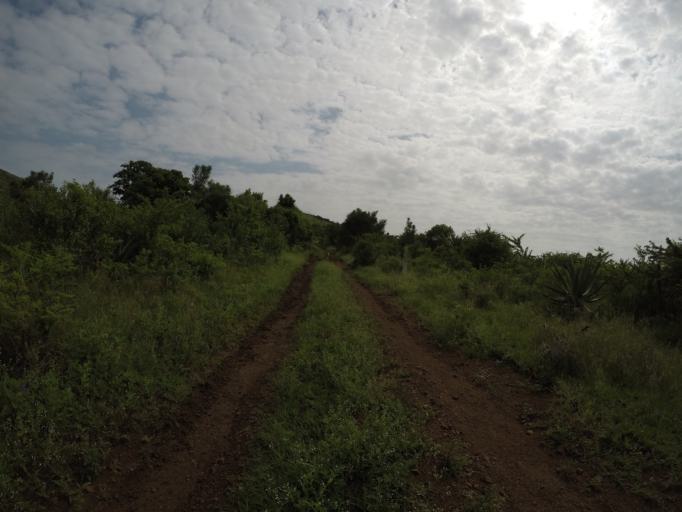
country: ZA
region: KwaZulu-Natal
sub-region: uThungulu District Municipality
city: Empangeni
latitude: -28.6232
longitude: 31.8944
